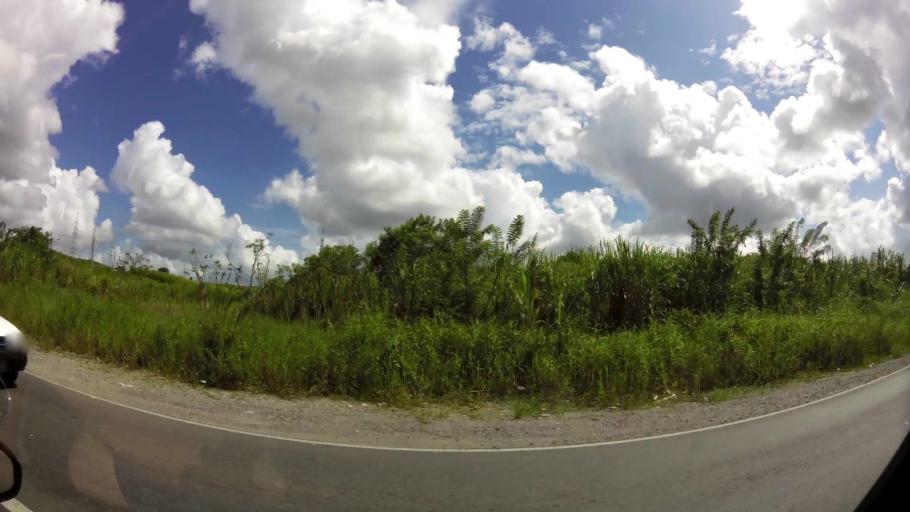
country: TT
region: Penal/Debe
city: Debe
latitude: 10.2199
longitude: -61.4640
